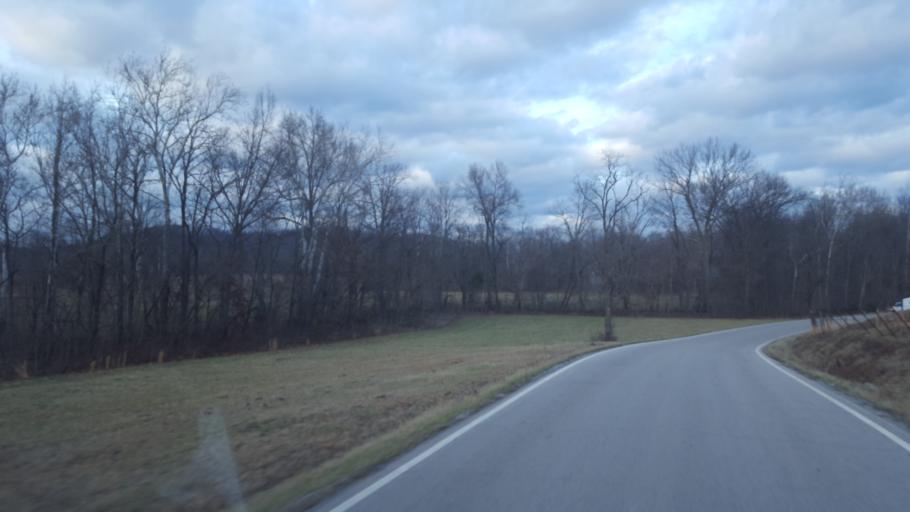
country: US
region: Kentucky
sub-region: Fleming County
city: Flemingsburg
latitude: 38.4976
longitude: -83.5582
